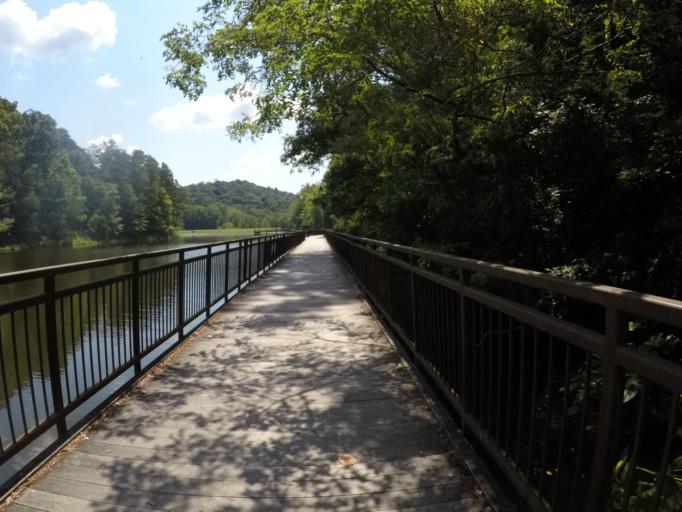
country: US
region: Ohio
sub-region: Lawrence County
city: Ironton
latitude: 38.6085
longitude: -82.6339
